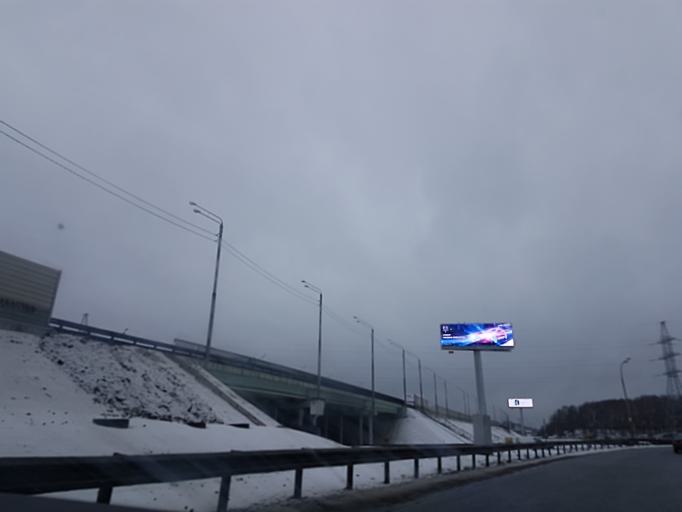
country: RU
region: Moskovskaya
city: Krasnogorsk
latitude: 55.8019
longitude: 37.3237
